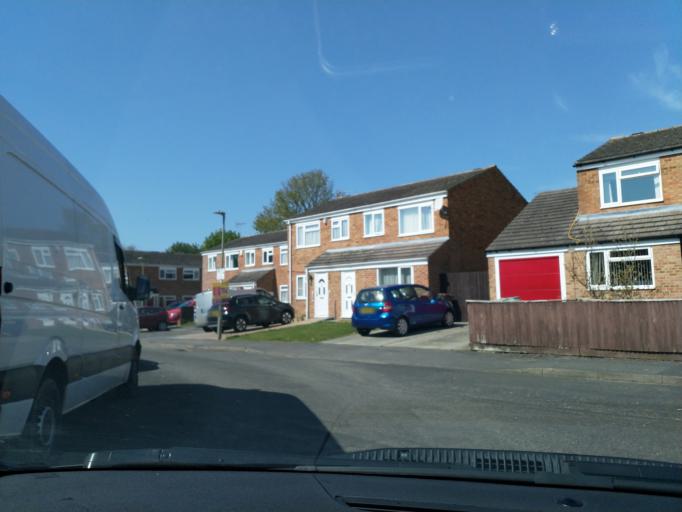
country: GB
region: England
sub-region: Oxfordshire
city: Cowley
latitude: 51.7402
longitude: -1.2002
